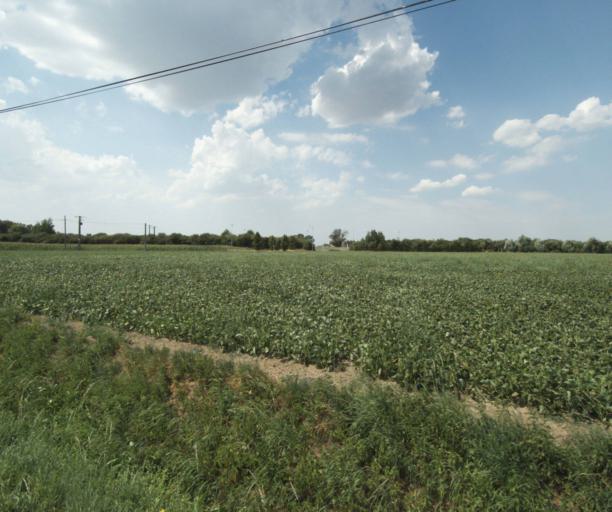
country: FR
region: Nord-Pas-de-Calais
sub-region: Departement du Nord
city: Comines
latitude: 50.7580
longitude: 3.0299
